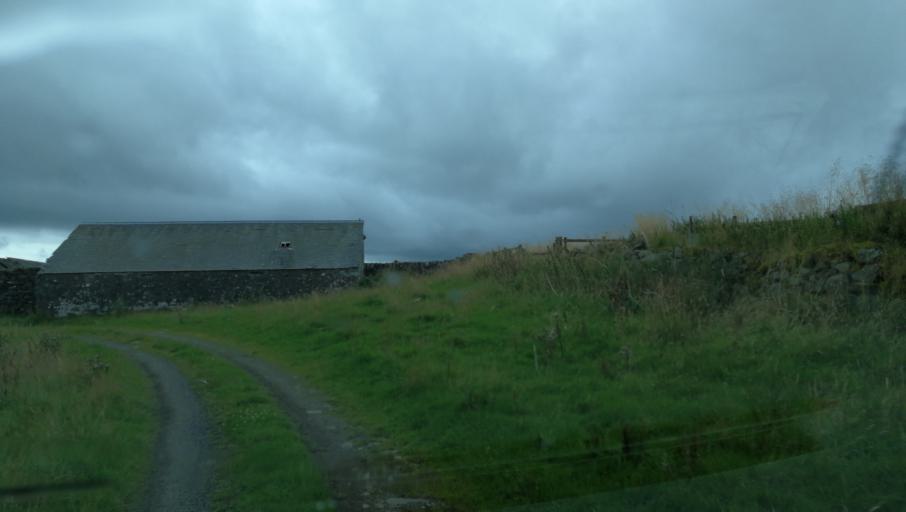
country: GB
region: Scotland
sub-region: Perth and Kinross
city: Blairgowrie
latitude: 56.6683
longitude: -3.3478
